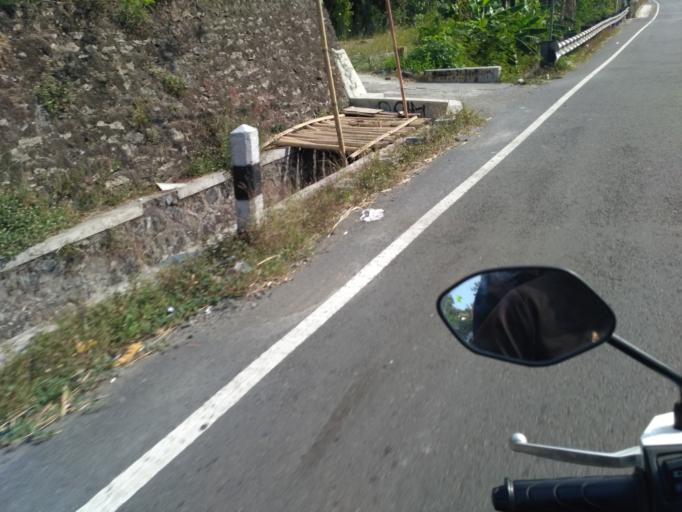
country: ID
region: Daerah Istimewa Yogyakarta
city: Godean
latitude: -7.8115
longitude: 110.2754
